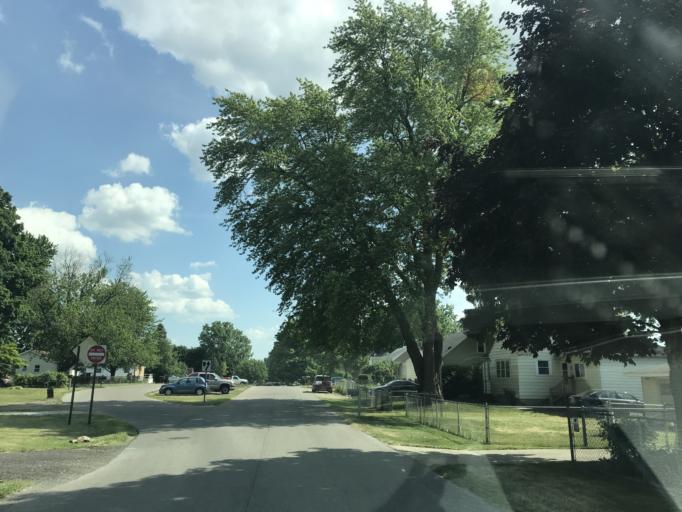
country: US
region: Michigan
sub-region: Washtenaw County
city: Ypsilanti
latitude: 42.2520
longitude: -83.5820
